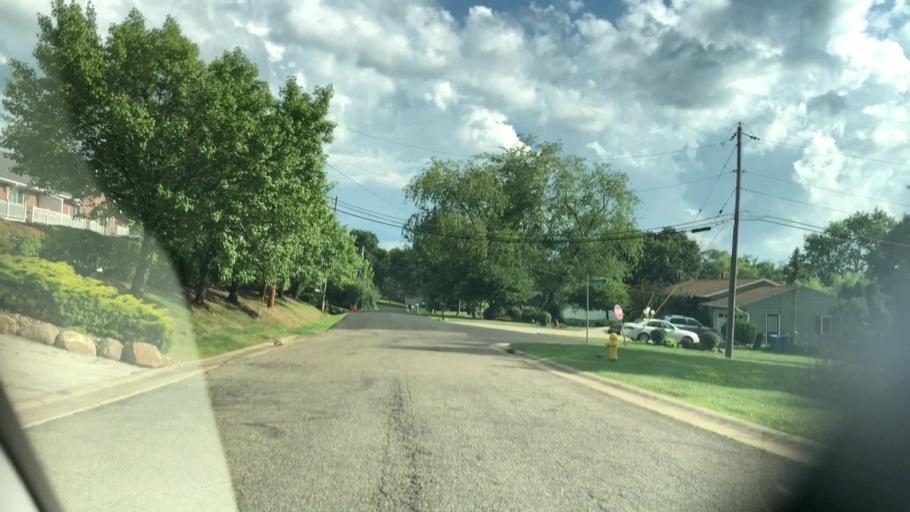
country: US
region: Ohio
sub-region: Summit County
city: Norton
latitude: 41.0298
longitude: -81.6322
